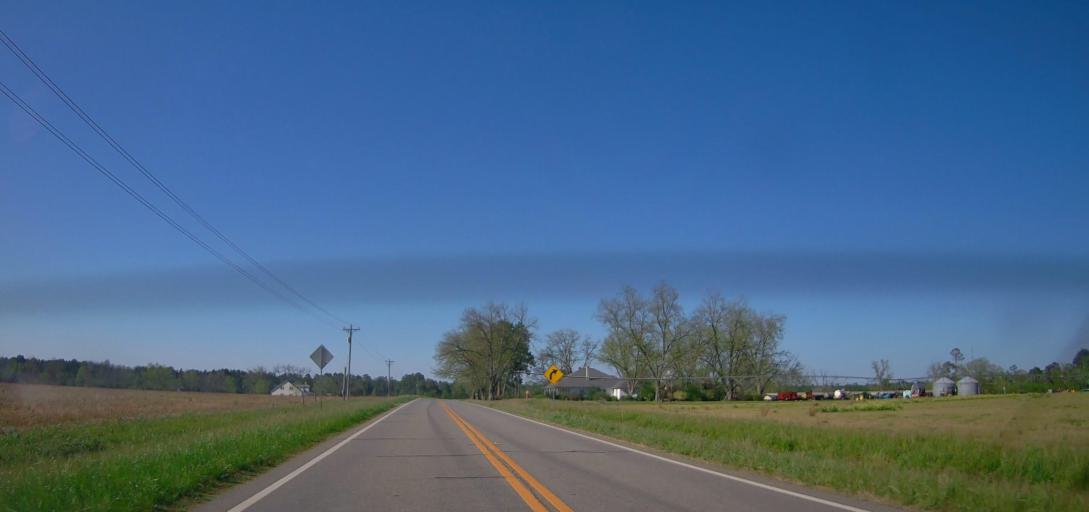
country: US
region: Georgia
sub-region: Wilcox County
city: Rochelle
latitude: 31.9230
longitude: -83.4661
